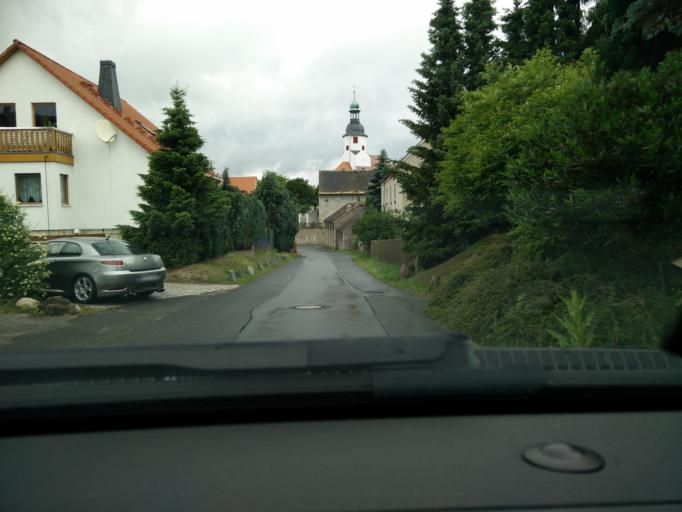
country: DE
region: Saxony
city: Bad Lausick
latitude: 51.1358
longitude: 12.6914
